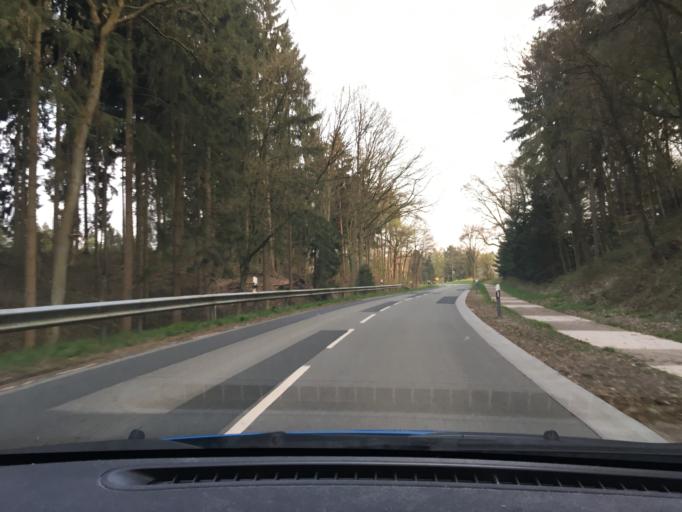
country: DE
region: Lower Saxony
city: Oldendorf
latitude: 53.1643
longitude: 10.2476
